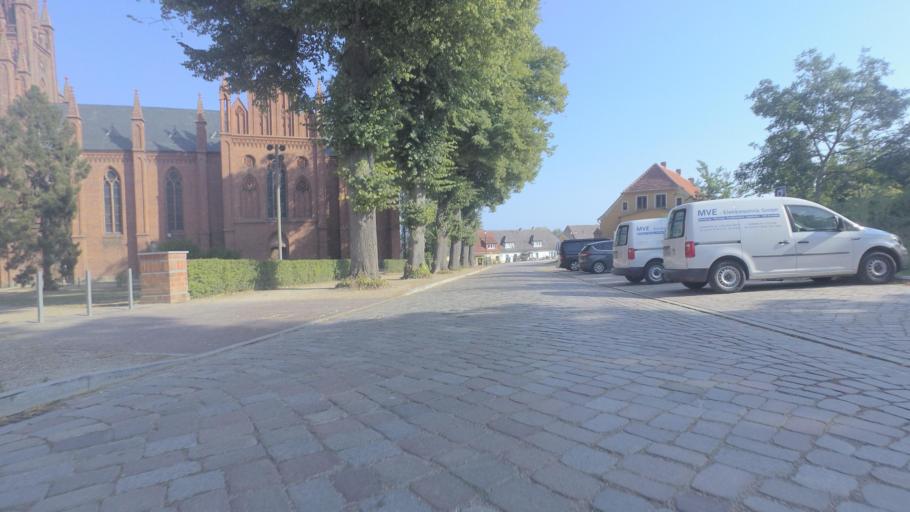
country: DE
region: Mecklenburg-Vorpommern
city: Malchow
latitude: 53.4714
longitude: 12.4325
